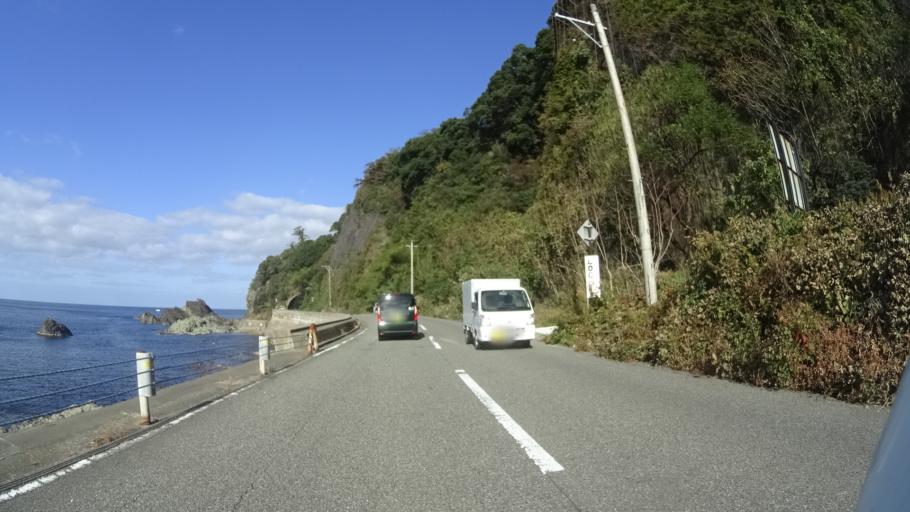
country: JP
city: Asahi
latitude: 35.9578
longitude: 135.9761
